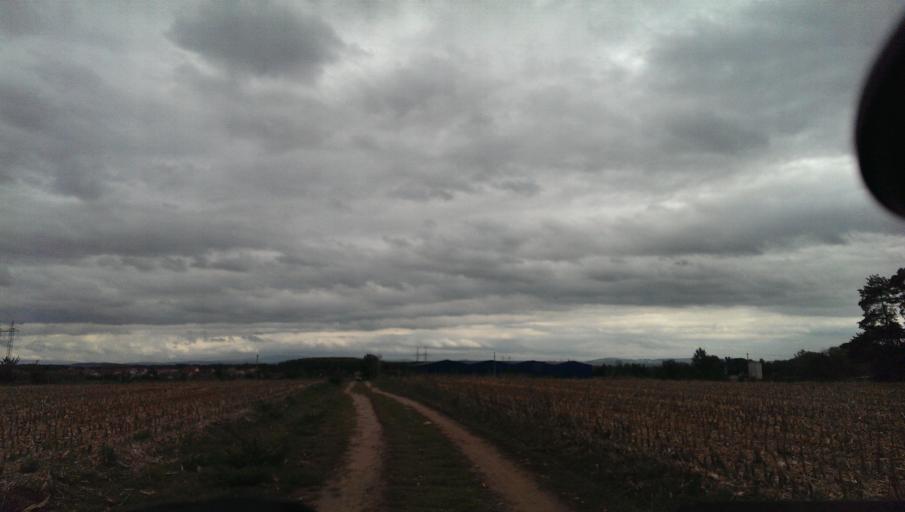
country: CZ
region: South Moravian
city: Moravsky Pisek
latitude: 48.9882
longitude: 17.3165
